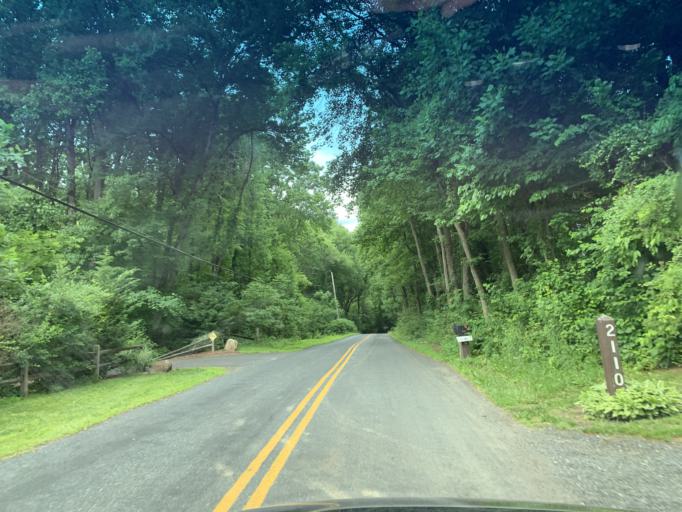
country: US
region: Maryland
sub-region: Harford County
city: Jarrettsville
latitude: 39.6210
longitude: -76.5011
